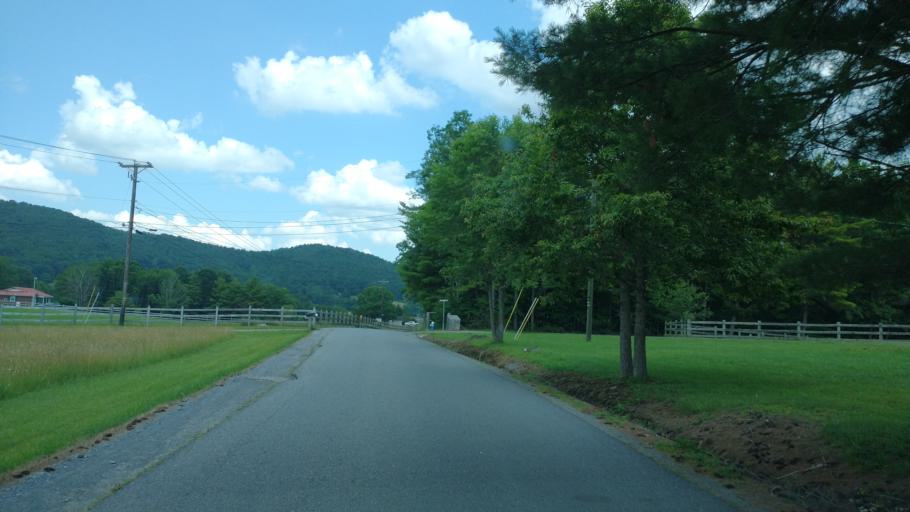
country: US
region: West Virginia
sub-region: Mercer County
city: Athens
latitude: 37.4578
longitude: -81.0175
